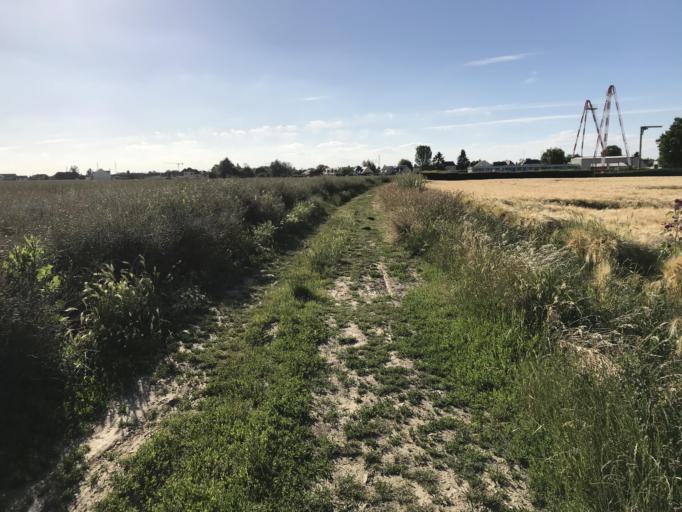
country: FR
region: Ile-de-France
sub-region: Departement de l'Essonne
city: Villejust
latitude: 48.6700
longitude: 2.2212
